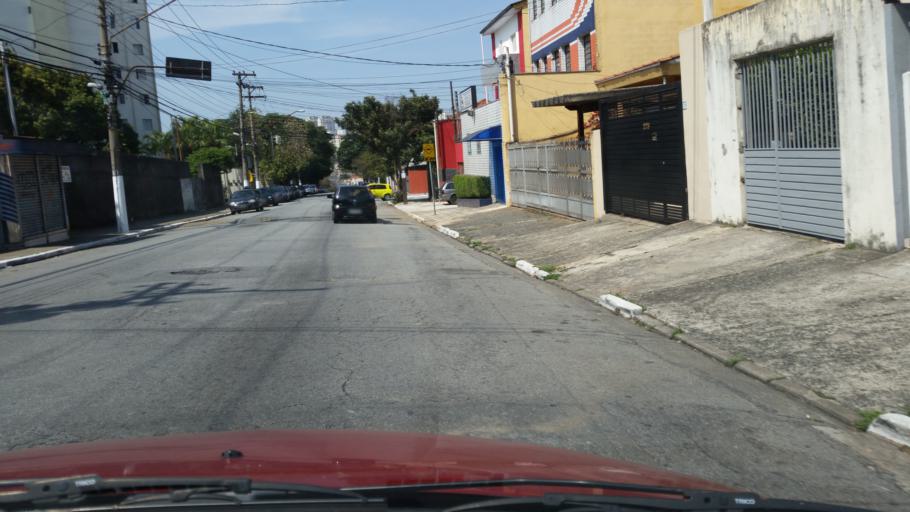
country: BR
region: Sao Paulo
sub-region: Diadema
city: Diadema
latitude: -23.6229
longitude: -46.6180
